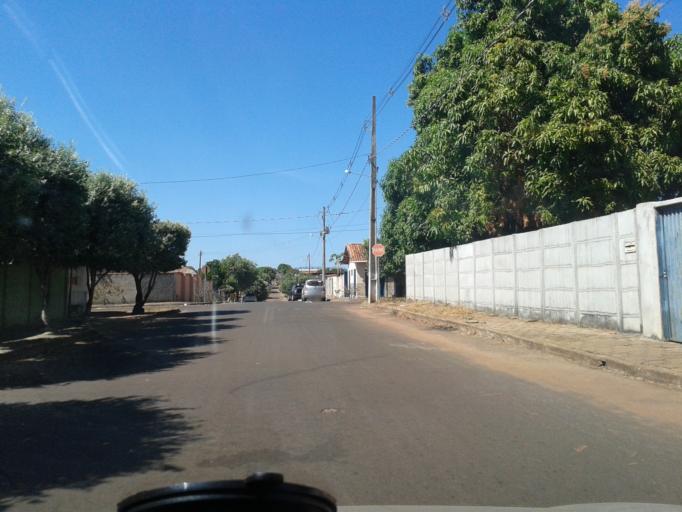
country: BR
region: Goias
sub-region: Sao Miguel Do Araguaia
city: Sao Miguel do Araguaia
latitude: -13.2784
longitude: -50.1576
